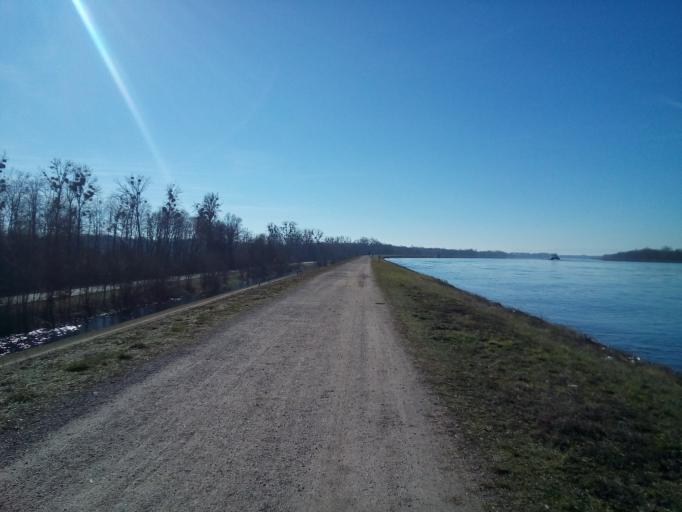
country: FR
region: Alsace
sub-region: Departement du Bas-Rhin
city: Gambsheim
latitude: 48.6660
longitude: 7.8974
